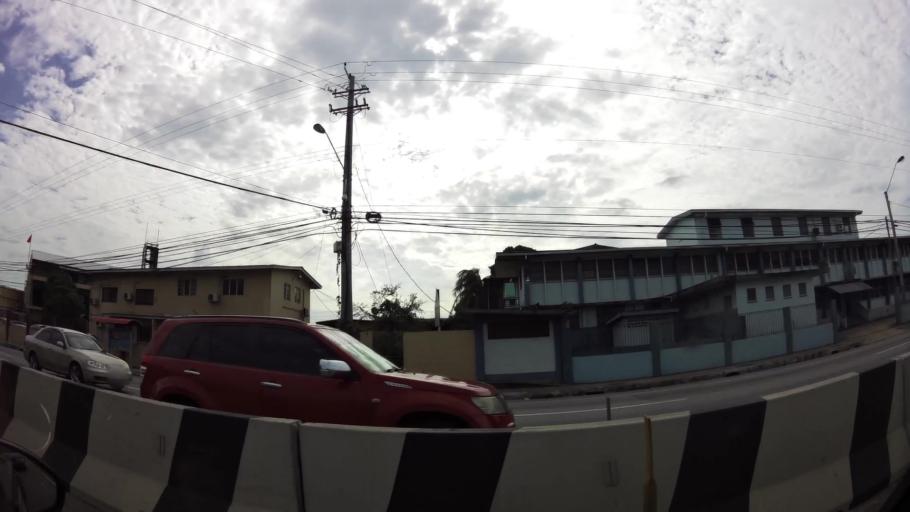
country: TT
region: City of Port of Spain
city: Port-of-Spain
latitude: 10.6538
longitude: -61.5172
